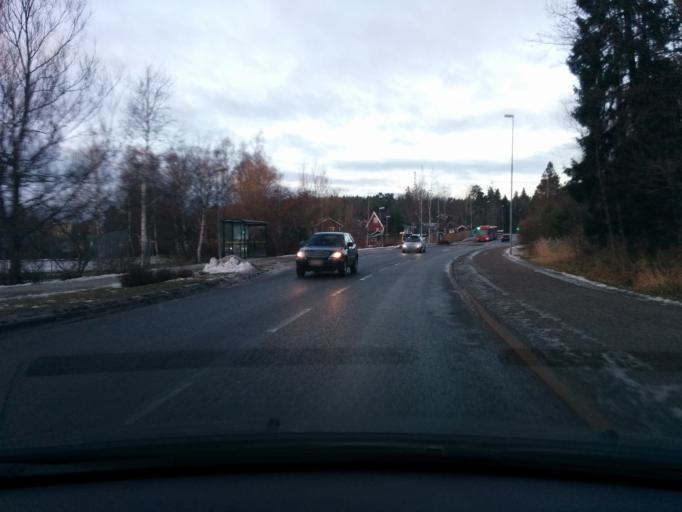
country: SE
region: Stockholm
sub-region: Nacka Kommun
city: Alta
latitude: 59.2726
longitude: 18.1767
